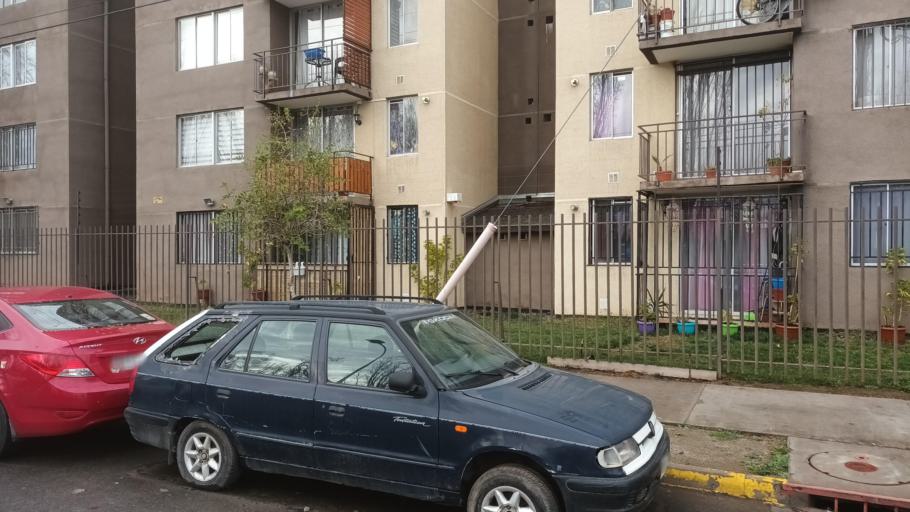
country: CL
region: Santiago Metropolitan
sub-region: Provincia de Santiago
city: La Pintana
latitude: -33.5576
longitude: -70.6296
